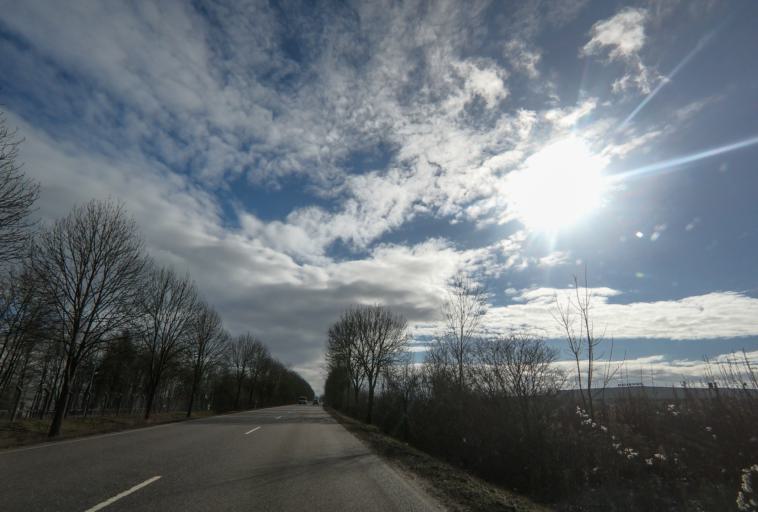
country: DE
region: Bavaria
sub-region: Upper Palatinate
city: Obertraubling
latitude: 48.9779
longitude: 12.1604
